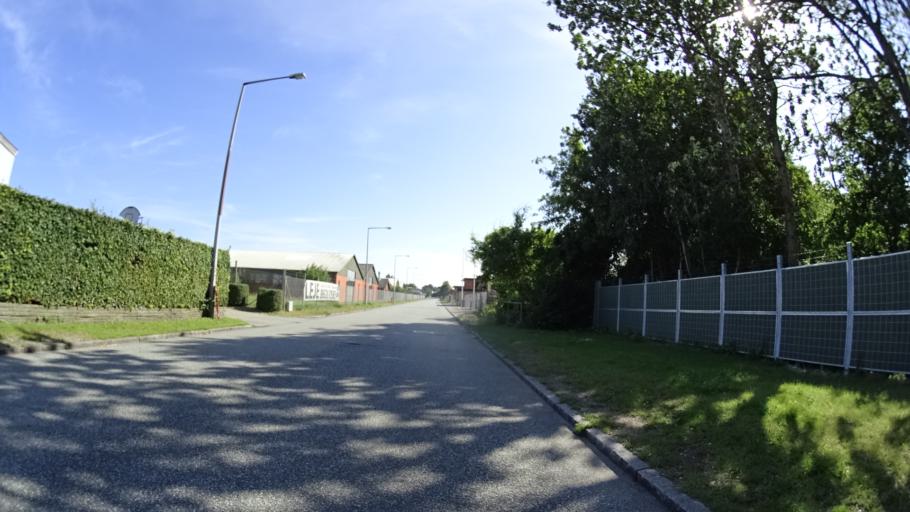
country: DK
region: Central Jutland
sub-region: Arhus Kommune
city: Stavtrup
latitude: 56.1451
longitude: 10.1474
